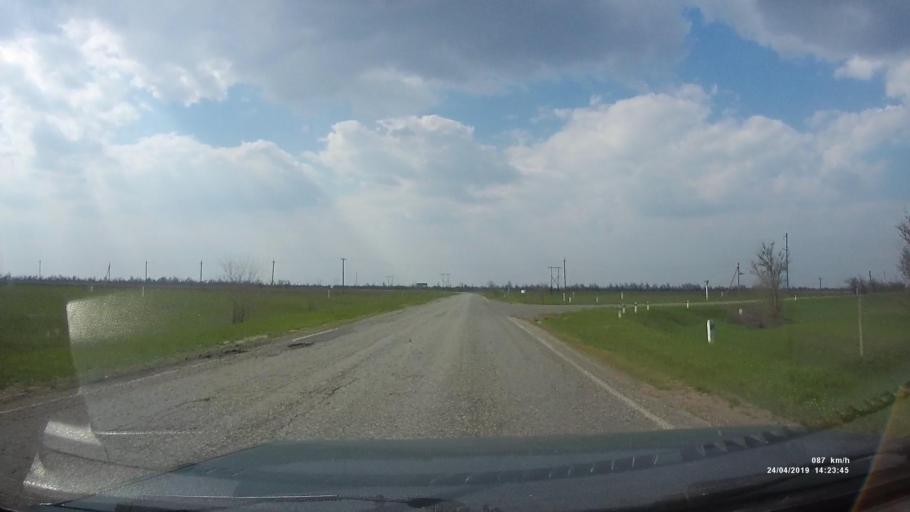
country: RU
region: Kalmykiya
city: Arshan'
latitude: 46.3250
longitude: 44.1087
